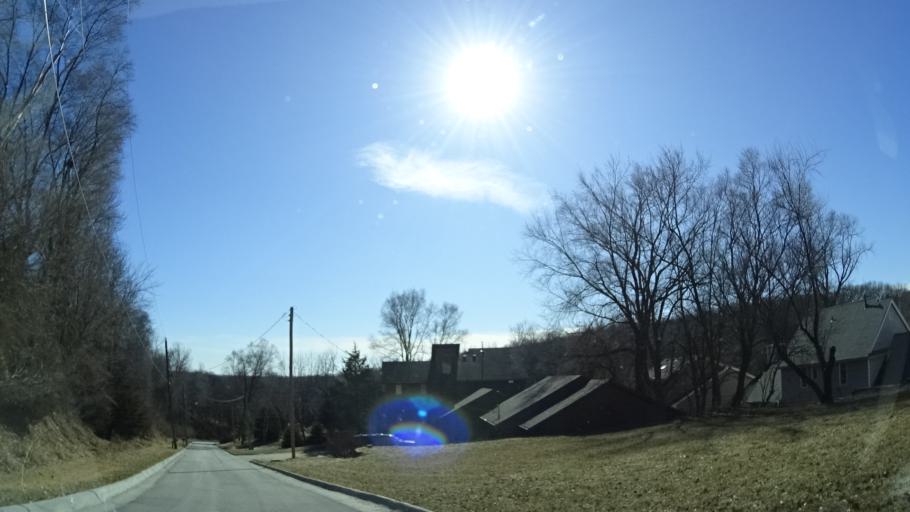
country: US
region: Nebraska
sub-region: Sarpy County
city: Bellevue
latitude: 41.1541
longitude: -95.8925
